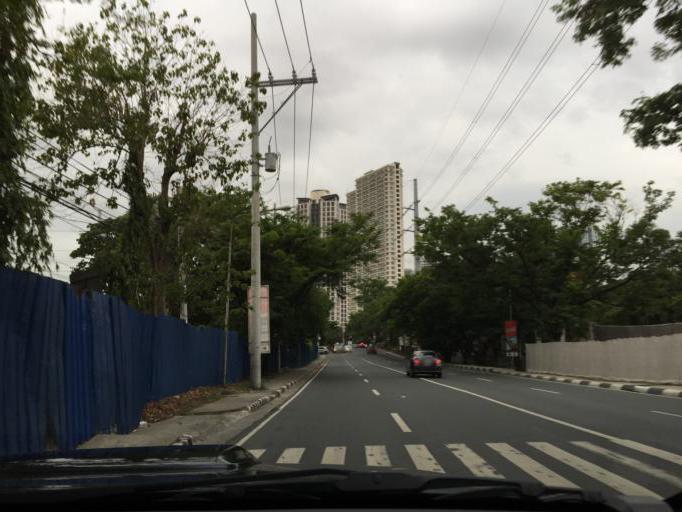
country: PH
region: Metro Manila
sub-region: Makati City
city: Makati City
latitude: 14.5388
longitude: 121.0471
